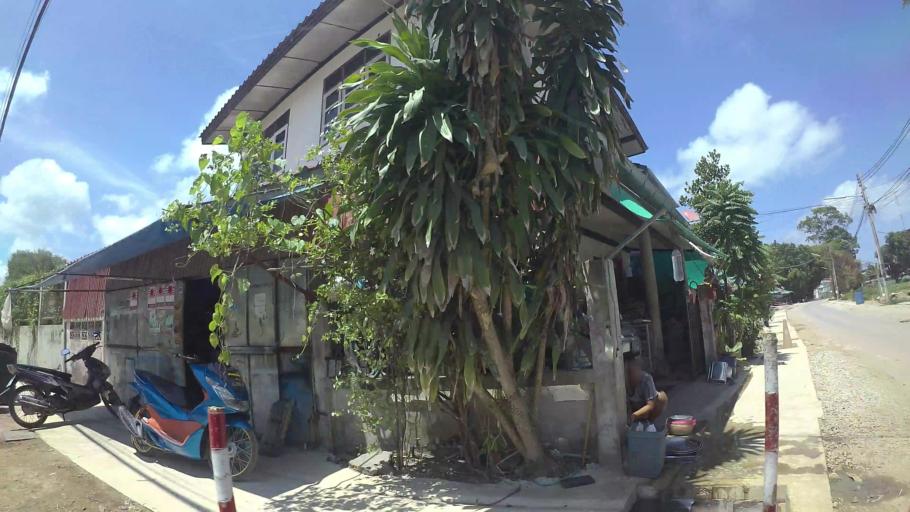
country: TH
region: Rayong
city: Rayong
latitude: 12.6884
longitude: 101.2652
